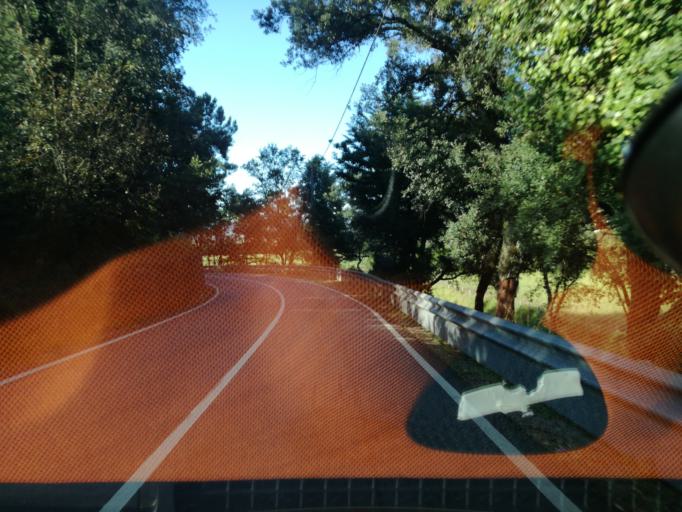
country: PT
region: Porto
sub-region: Santo Tirso
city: Sao Miguel do Couto
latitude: 41.3109
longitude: -8.4608
